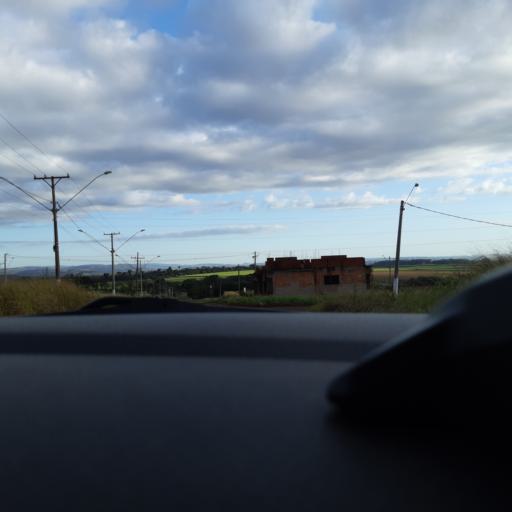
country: BR
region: Sao Paulo
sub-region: Ourinhos
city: Ourinhos
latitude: -22.9993
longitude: -49.8443
